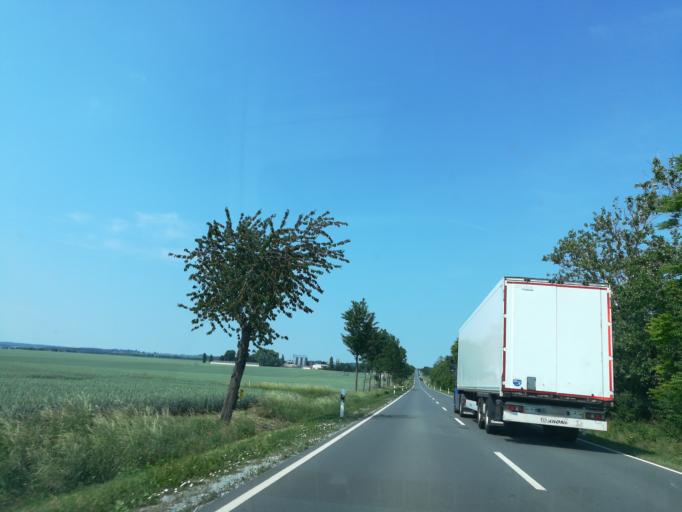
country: DE
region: Saxony-Anhalt
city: Aschersleben
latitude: 51.7905
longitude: 11.4590
